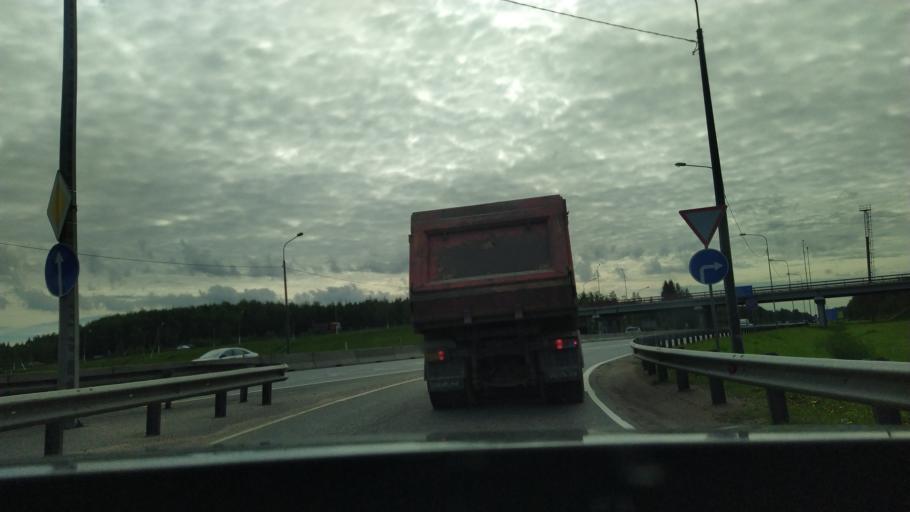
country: RU
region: Leningrad
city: Ul'yanovka
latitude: 59.6065
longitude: 30.7570
